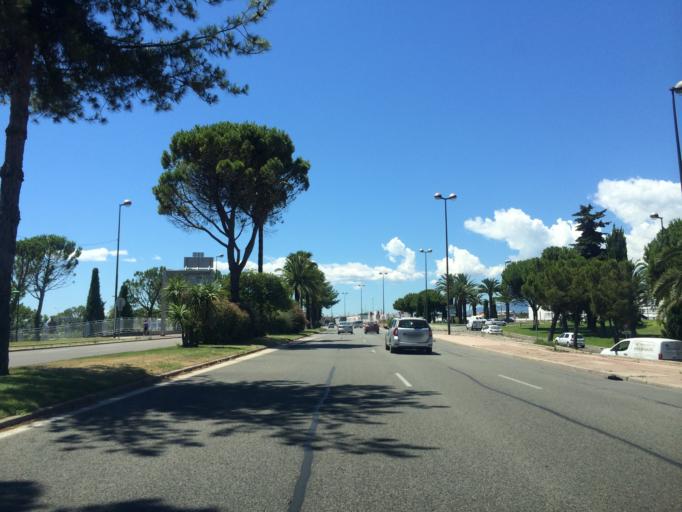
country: FR
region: Provence-Alpes-Cote d'Azur
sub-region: Departement des Alpes-Maritimes
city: Saint-Laurent-du-Var
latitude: 43.6657
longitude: 7.2056
